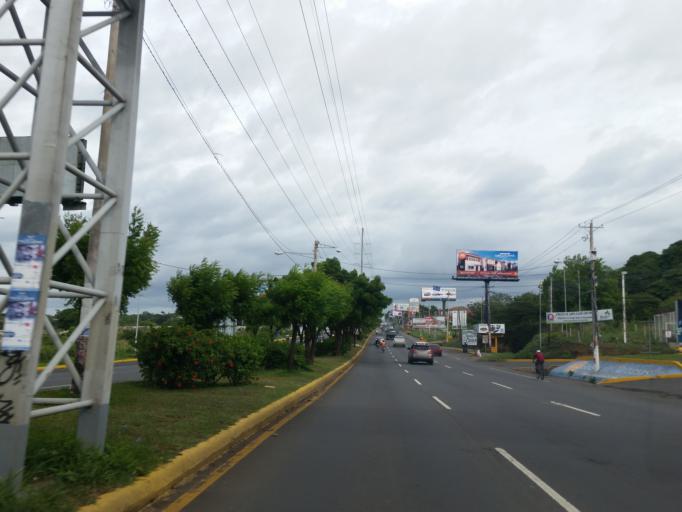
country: NI
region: Managua
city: Managua
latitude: 12.1047
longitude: -86.2476
